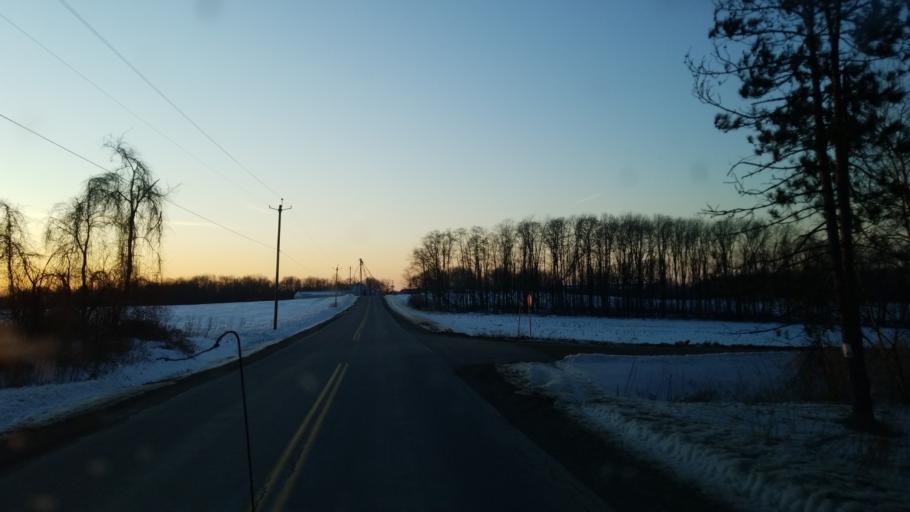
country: US
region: New York
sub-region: Allegany County
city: Andover
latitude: 42.0078
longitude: -77.7006
